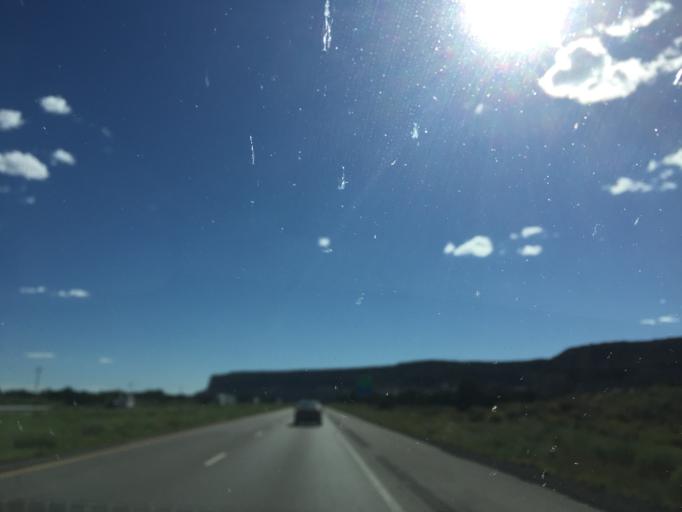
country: US
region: Arizona
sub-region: Apache County
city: Houck
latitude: 35.3792
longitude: -109.0240
